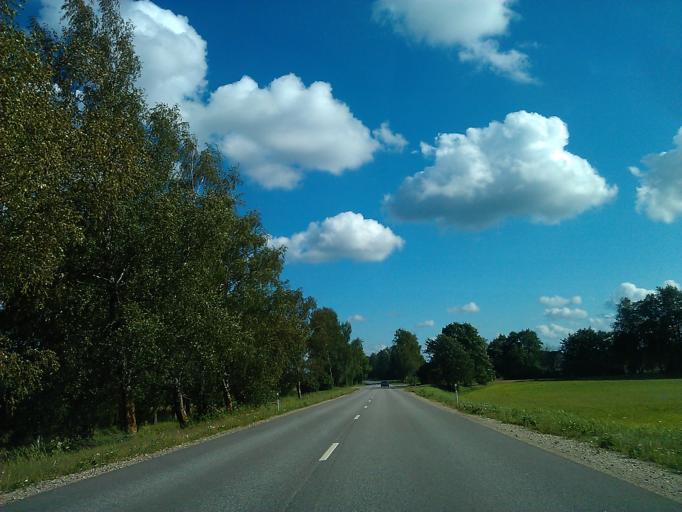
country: LV
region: Rujienas
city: Rujiena
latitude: 57.8368
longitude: 25.3871
